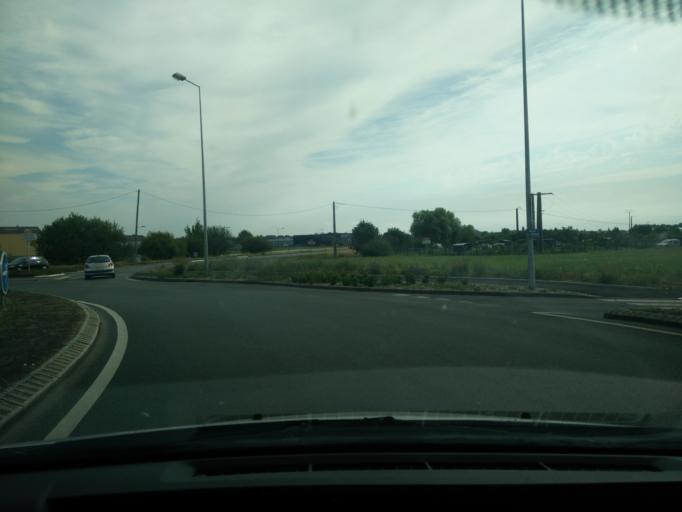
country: FR
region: Pays de la Loire
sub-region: Departement de Maine-et-Loire
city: Les Ponts-de-Ce
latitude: 47.4346
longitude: -0.4994
